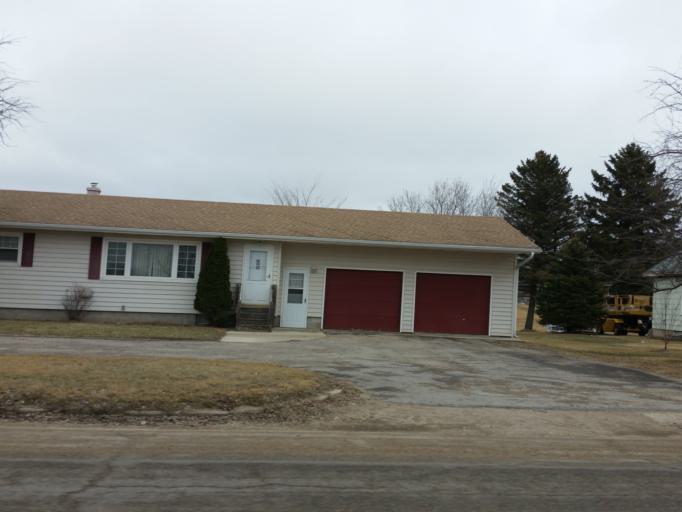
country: US
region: North Dakota
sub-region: Cass County
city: Casselton
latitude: 47.0999
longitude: -97.2181
